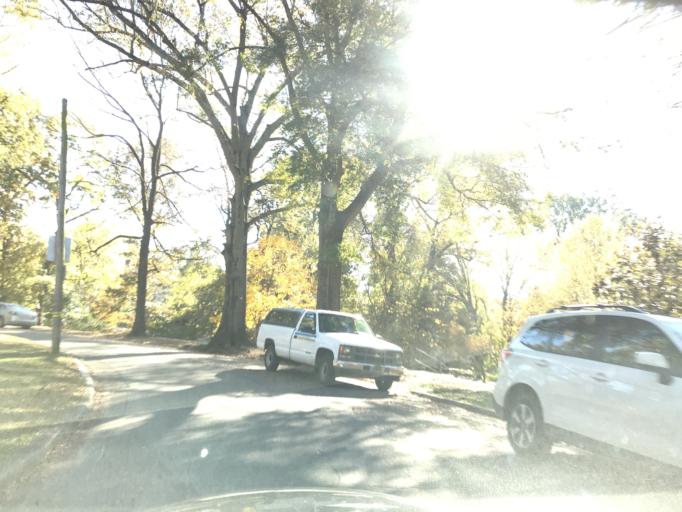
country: US
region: North Carolina
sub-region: Wake County
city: Raleigh
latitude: 35.7957
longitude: -78.6332
